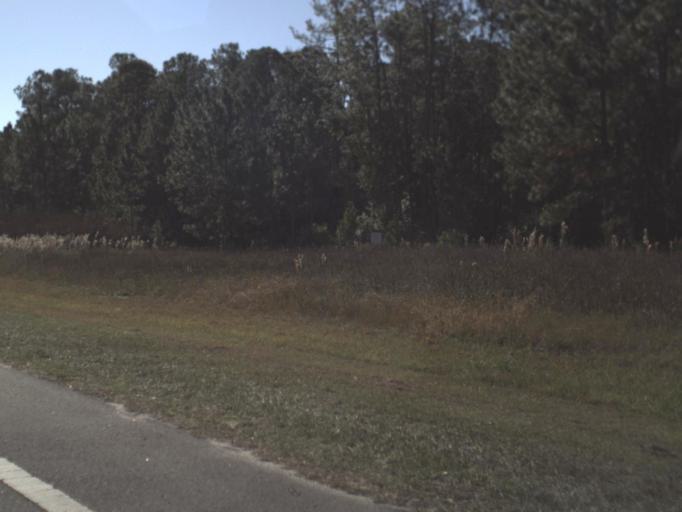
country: US
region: Florida
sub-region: Volusia County
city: South Daytona
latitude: 29.1561
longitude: -81.0657
